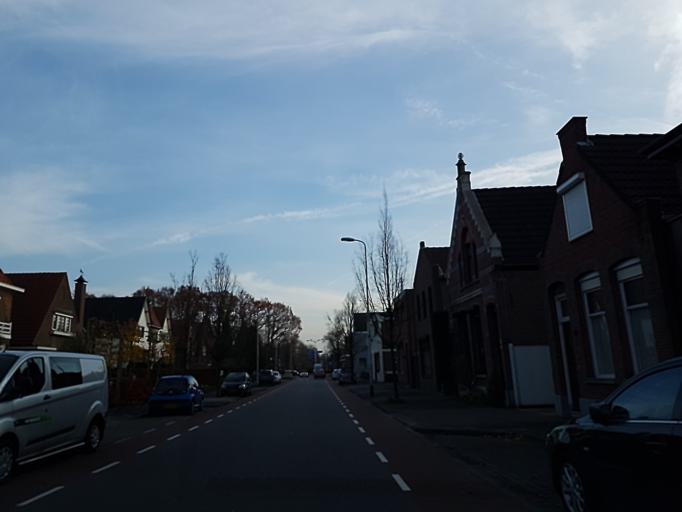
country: NL
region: North Brabant
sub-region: Roosendaal
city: Roosendaal
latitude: 51.5292
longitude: 4.4592
